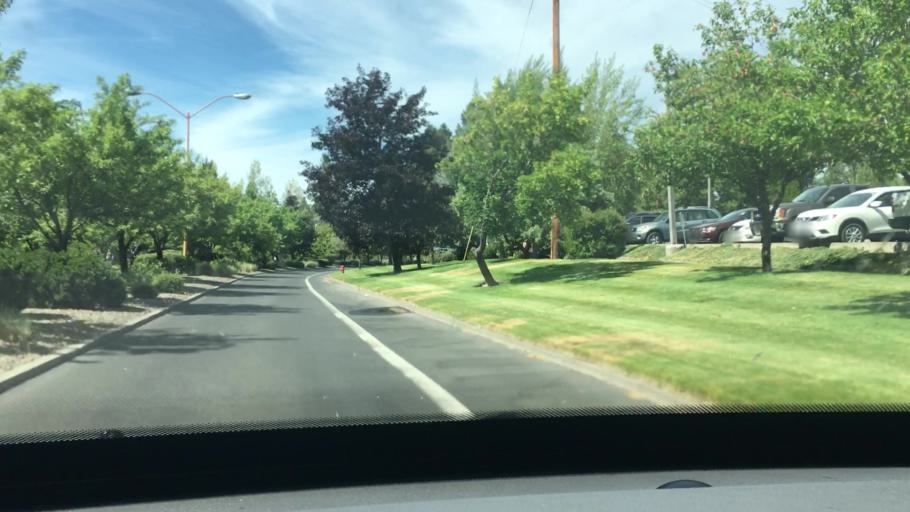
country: US
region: Oregon
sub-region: Deschutes County
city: Bend
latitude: 44.0434
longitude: -121.3271
